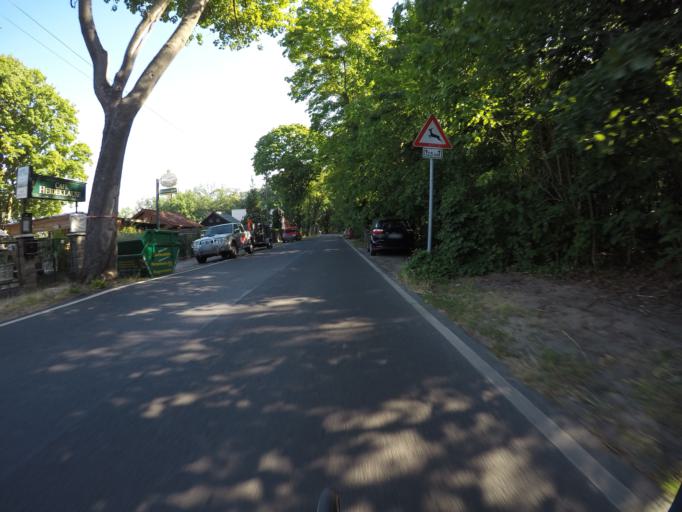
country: DE
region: Berlin
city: Schmockwitz
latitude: 52.3481
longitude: 13.6456
